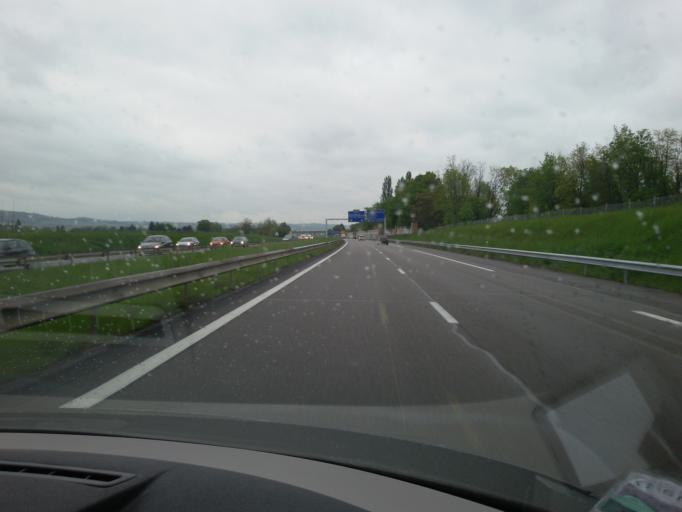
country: FR
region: Rhone-Alpes
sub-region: Departement du Rhone
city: Les Cheres
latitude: 45.8810
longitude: 4.7391
